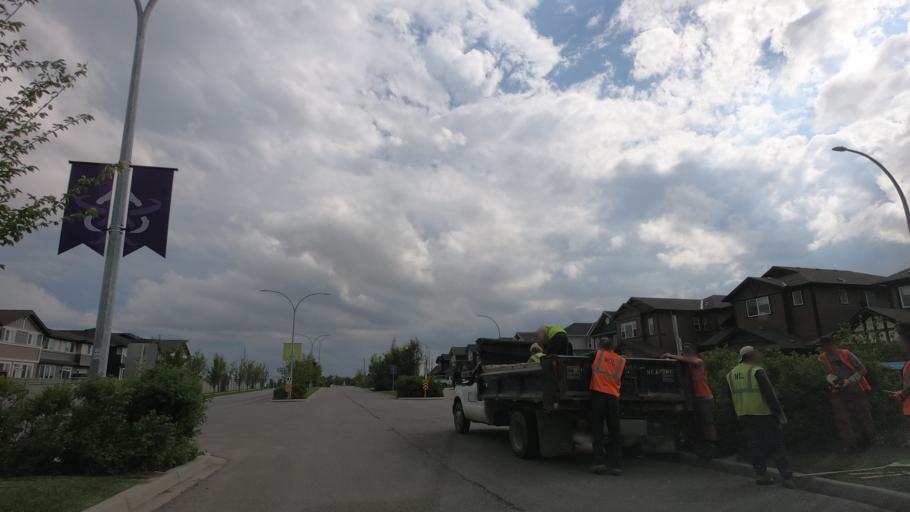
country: CA
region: Alberta
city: Airdrie
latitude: 51.2578
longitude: -113.9919
